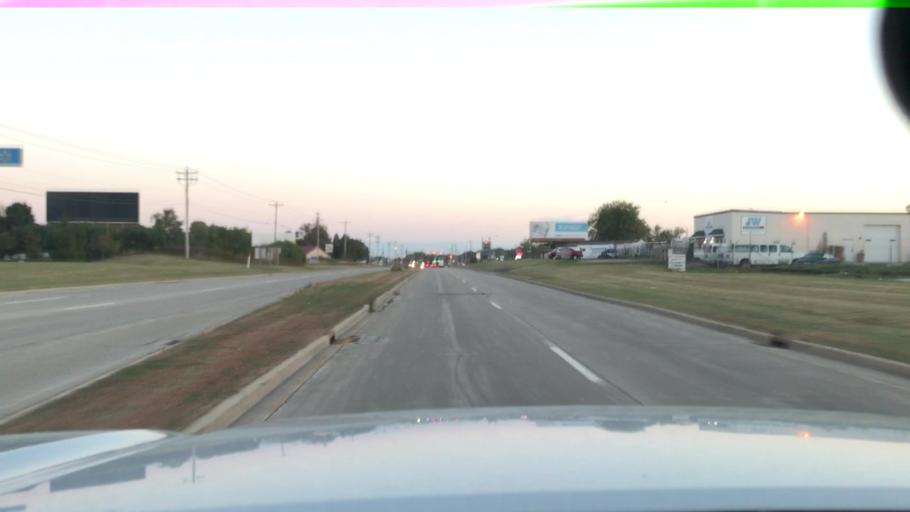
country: US
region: Wisconsin
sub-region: Brown County
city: Allouez
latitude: 44.4784
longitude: -87.9691
